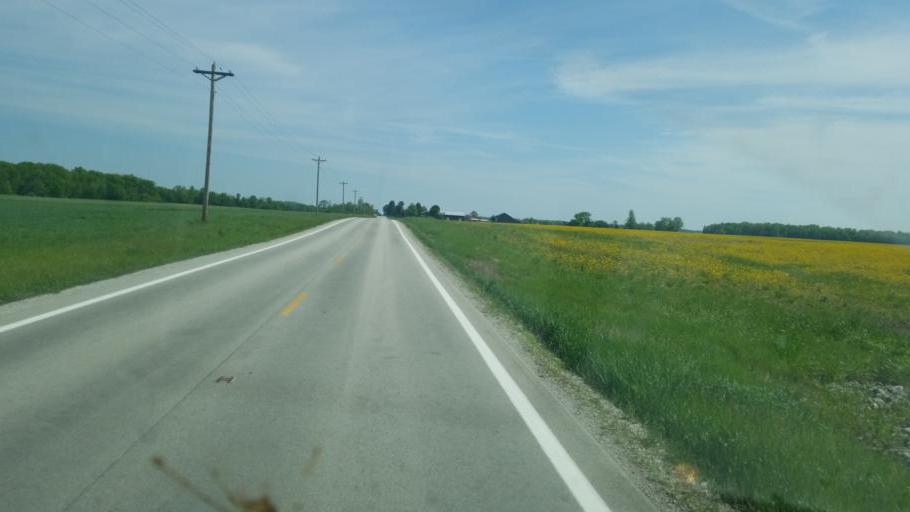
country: US
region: Ohio
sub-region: Seneca County
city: Tiffin
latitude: 41.0523
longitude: -83.0813
